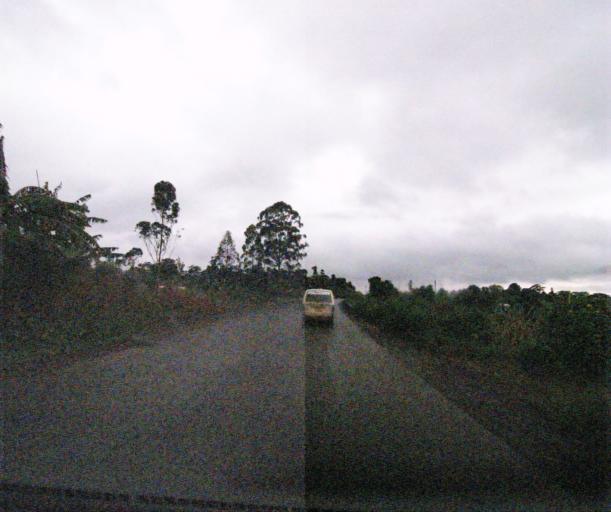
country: CM
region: West
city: Bansoa
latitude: 5.4982
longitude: 10.2519
